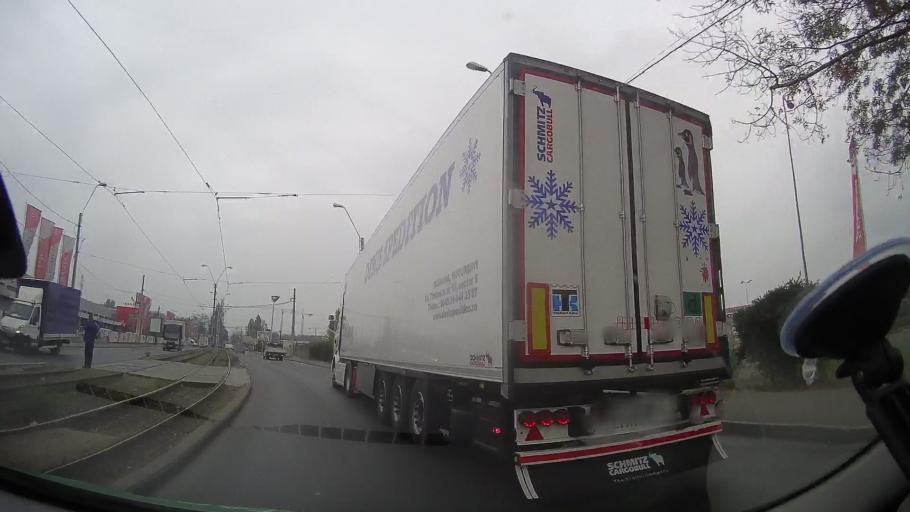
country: RO
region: Ilfov
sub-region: Comuna Chiajna
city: Rosu
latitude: 44.4240
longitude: 25.9993
